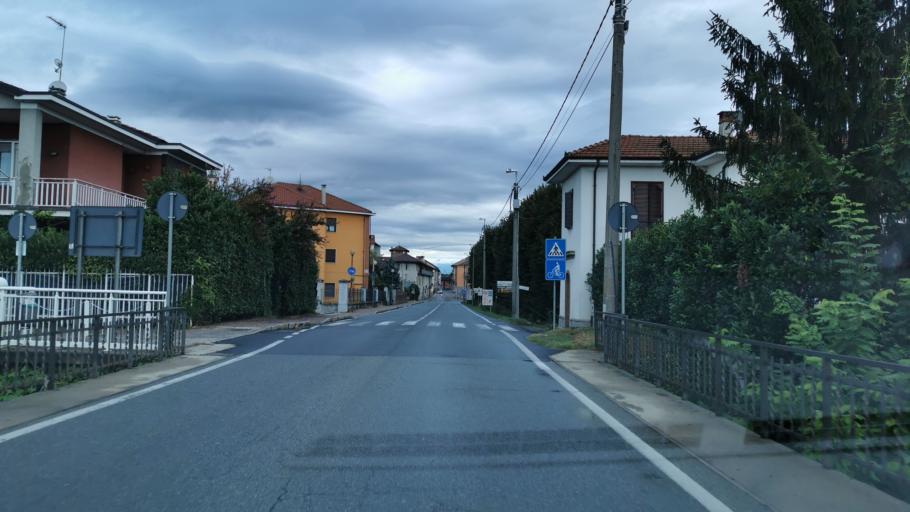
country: IT
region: Piedmont
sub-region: Provincia di Torino
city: San Benigno Canavese
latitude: 45.2199
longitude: 7.7832
